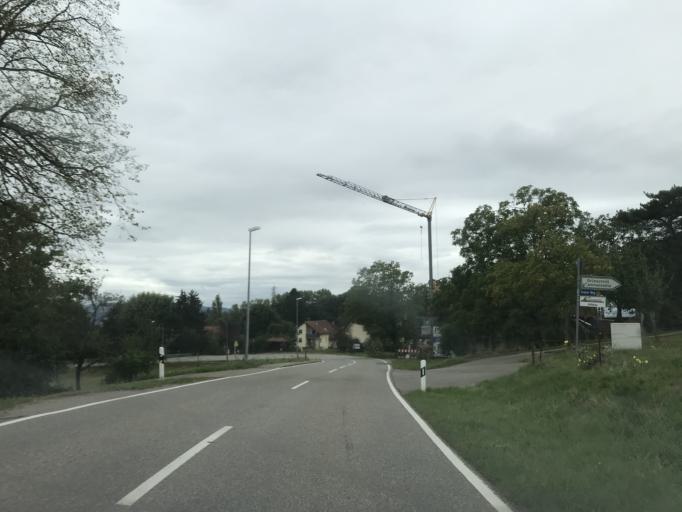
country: DE
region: Baden-Wuerttemberg
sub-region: Freiburg Region
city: Murg
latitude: 47.5728
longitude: 8.0363
